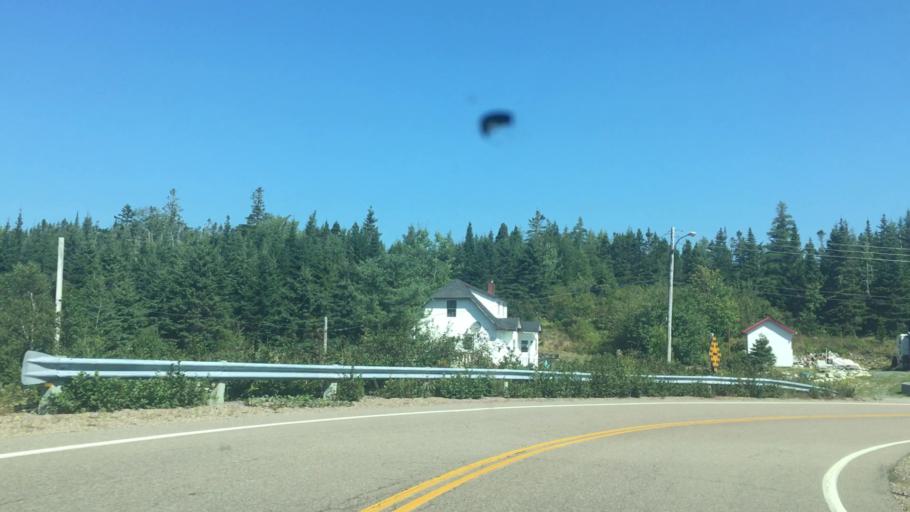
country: CA
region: Nova Scotia
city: Antigonish
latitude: 45.0279
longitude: -62.0310
